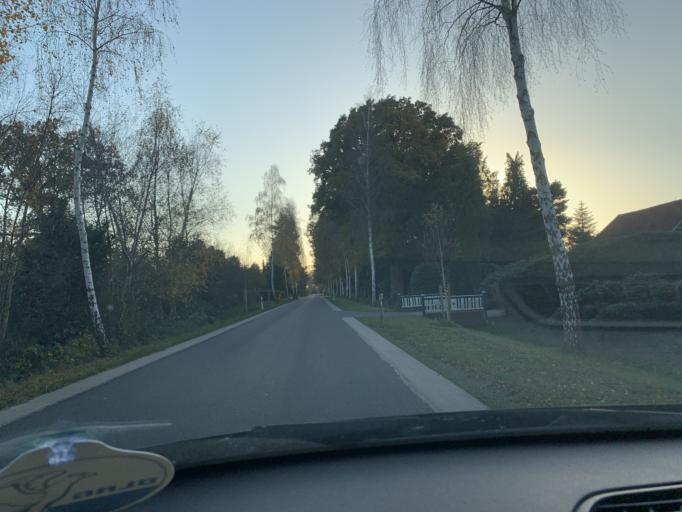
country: DE
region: Lower Saxony
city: Bad Zwischenahn
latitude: 53.1587
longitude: 8.0559
